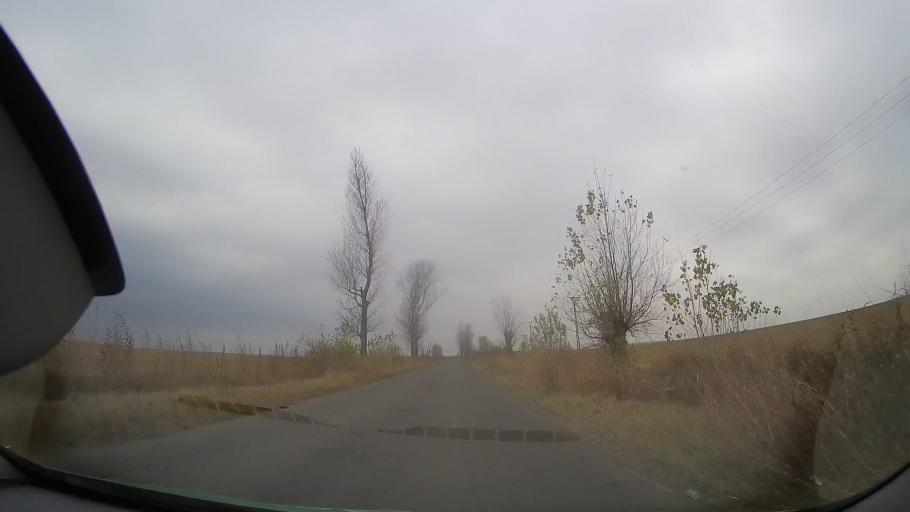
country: RO
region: Buzau
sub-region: Comuna Scutelnici
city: Scutelnici
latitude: 44.8817
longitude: 26.9507
